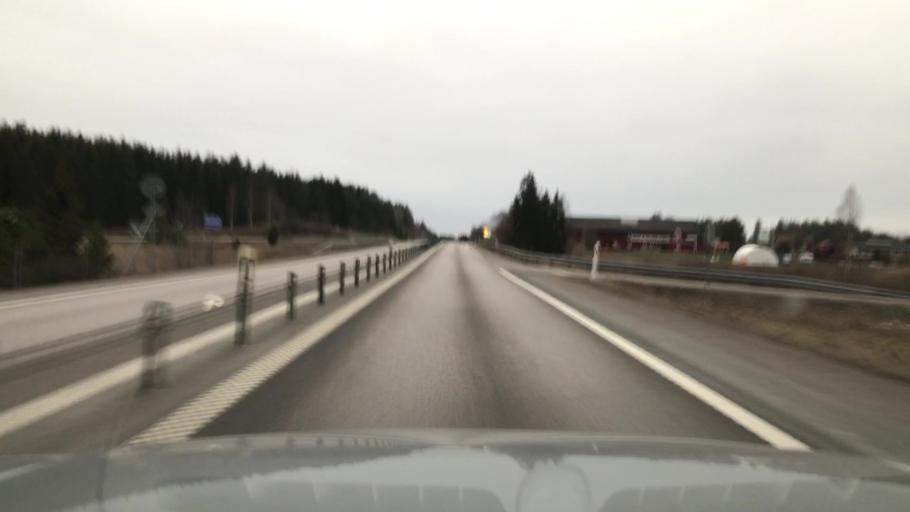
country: SE
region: OEstergoetland
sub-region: Valdemarsviks Kommun
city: Gusum
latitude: 58.2822
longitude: 16.5079
